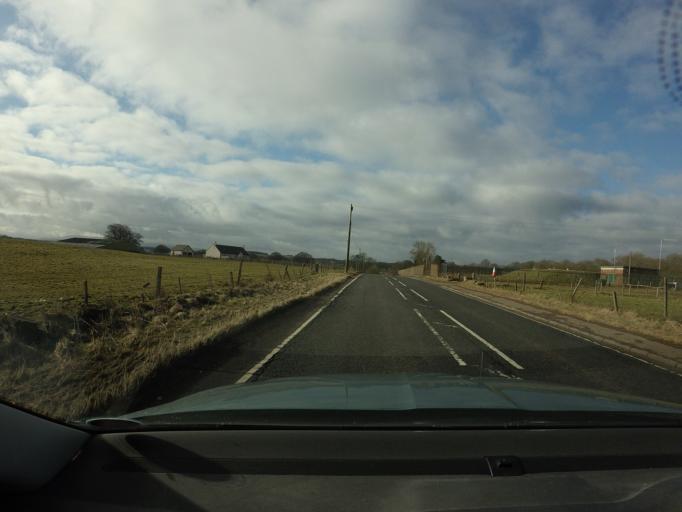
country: GB
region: Scotland
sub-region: South Lanarkshire
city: Forth
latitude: 55.7508
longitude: -3.7051
